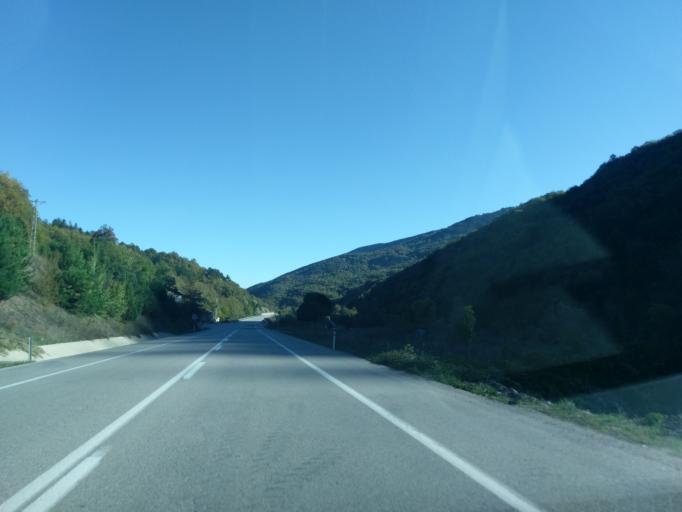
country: TR
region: Sinop
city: Erfelek
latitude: 41.7226
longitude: 34.9392
